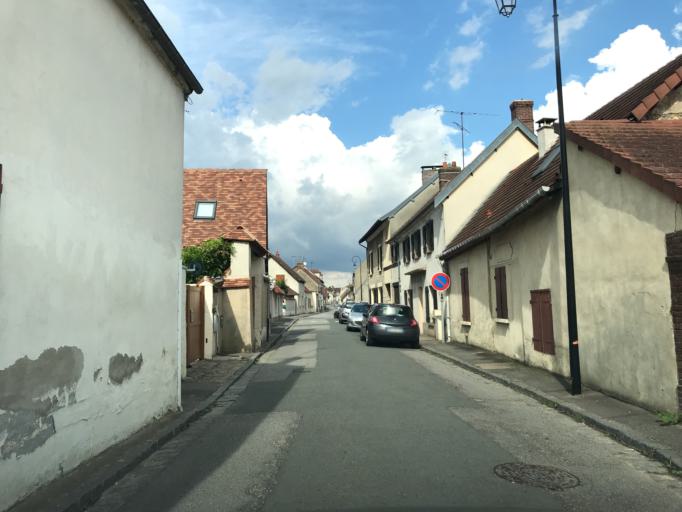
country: FR
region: Haute-Normandie
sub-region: Departement de l'Eure
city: Gasny
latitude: 49.0887
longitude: 1.5981
